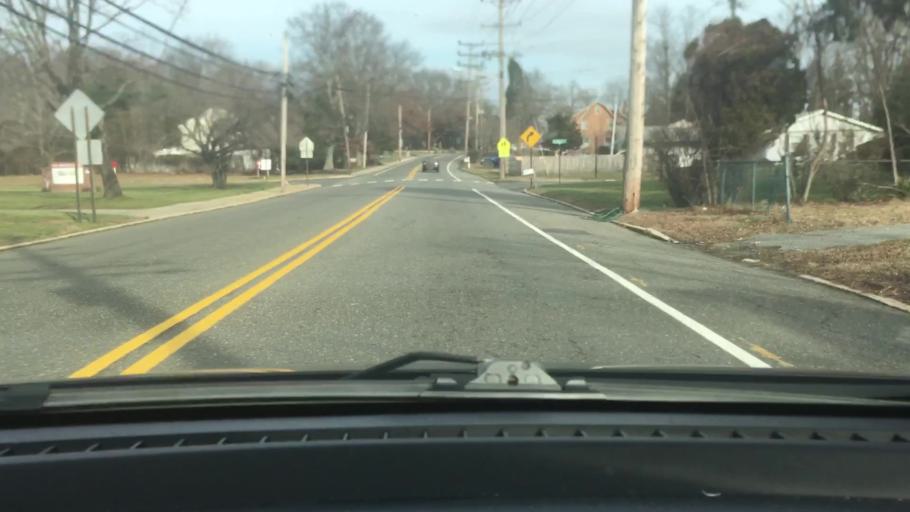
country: US
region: New Jersey
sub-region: Monmouth County
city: Shark River Hills
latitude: 40.2102
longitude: -74.0787
